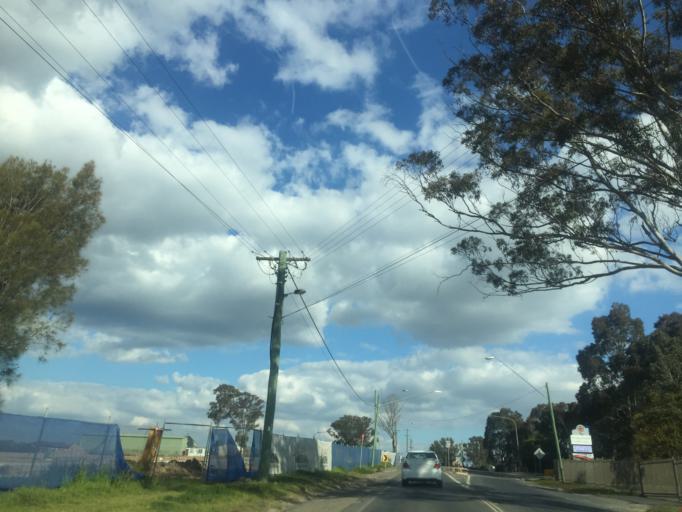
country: AU
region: New South Wales
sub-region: Blacktown
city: Quakers Hill
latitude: -33.7048
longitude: 150.8941
